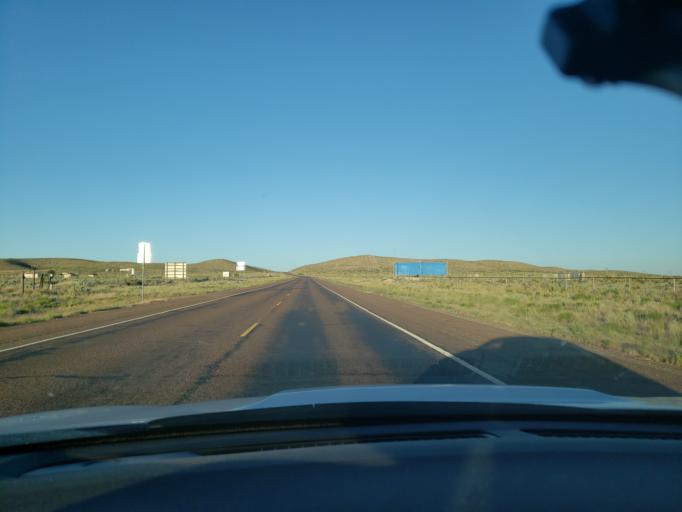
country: US
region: Texas
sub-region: El Paso County
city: Homestead Meadows South
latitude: 31.8267
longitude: -105.9072
